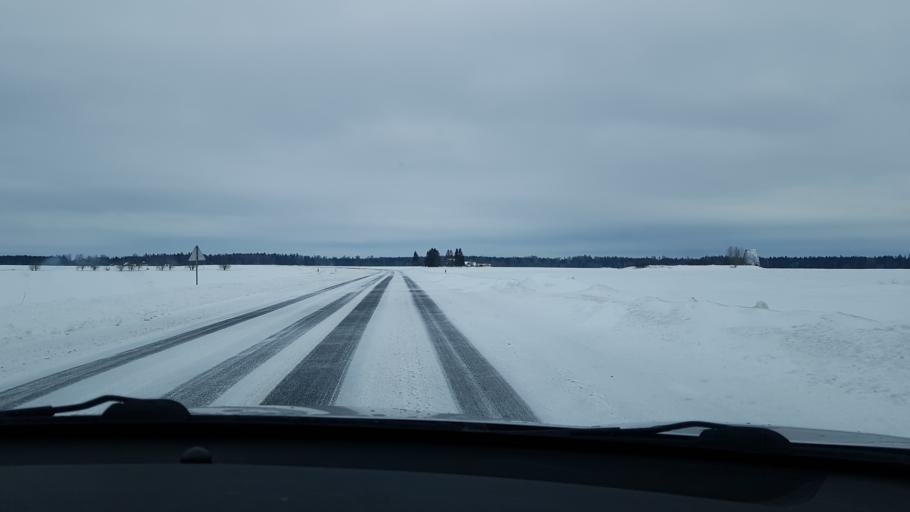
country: EE
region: Jaervamaa
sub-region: Jaerva-Jaani vald
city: Jarva-Jaani
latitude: 59.1147
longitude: 25.7941
